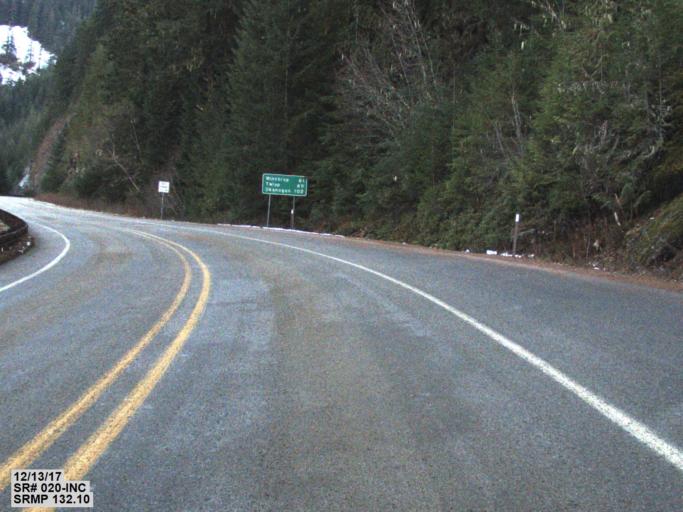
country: US
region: Washington
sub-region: Snohomish County
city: Darrington
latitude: 48.7080
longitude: -121.0891
